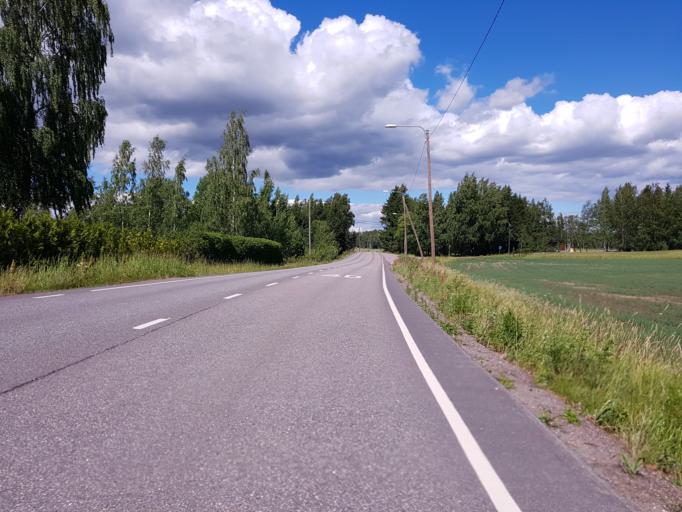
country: FI
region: Uusimaa
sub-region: Helsinki
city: Teekkarikylae
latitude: 60.3116
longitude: 24.8716
